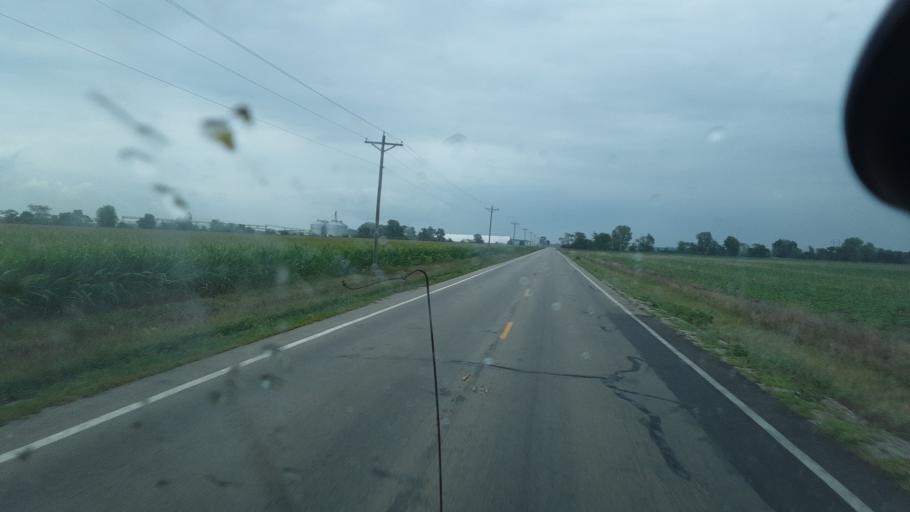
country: US
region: Ohio
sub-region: Defiance County
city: Hicksville
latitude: 41.2960
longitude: -84.7069
